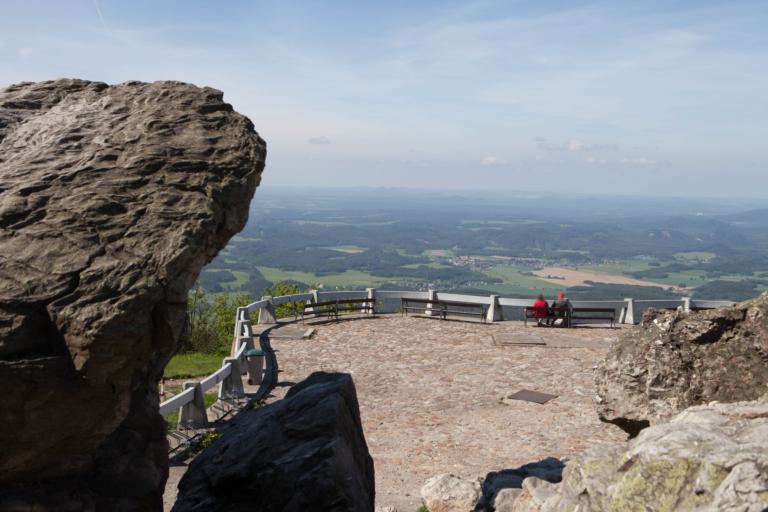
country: CZ
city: Straz nad Nisou
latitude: 50.7329
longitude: 14.9845
